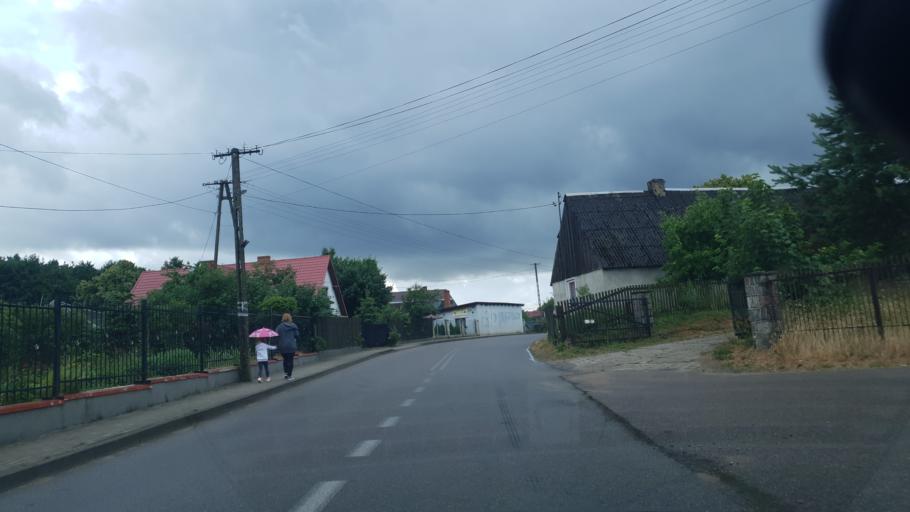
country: PL
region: Pomeranian Voivodeship
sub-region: Powiat kartuski
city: Stezyca
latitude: 54.2374
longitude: 17.9868
